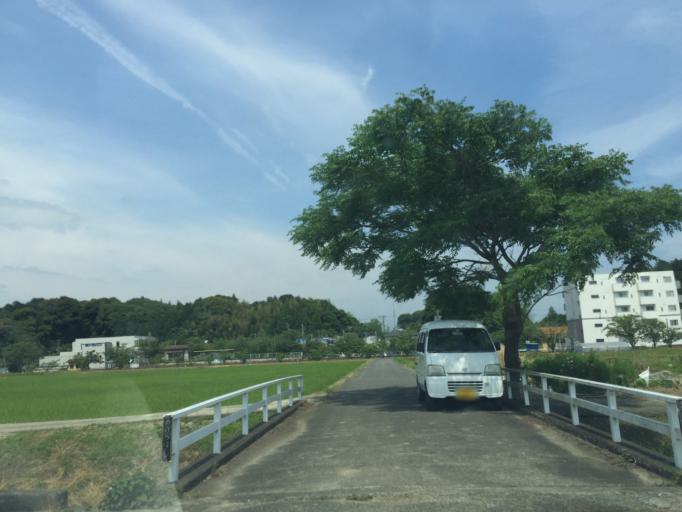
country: JP
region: Shizuoka
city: Mori
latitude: 34.7873
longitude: 137.9626
